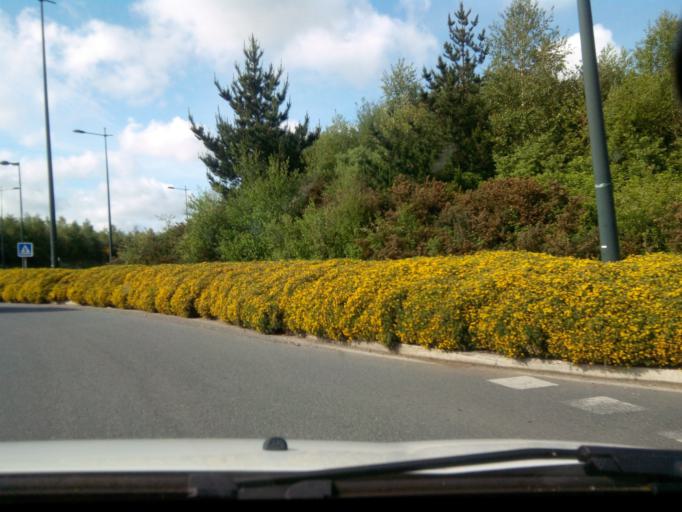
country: FR
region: Brittany
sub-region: Departement des Cotes-d'Armor
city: Lannion
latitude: 48.7513
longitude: -3.4486
